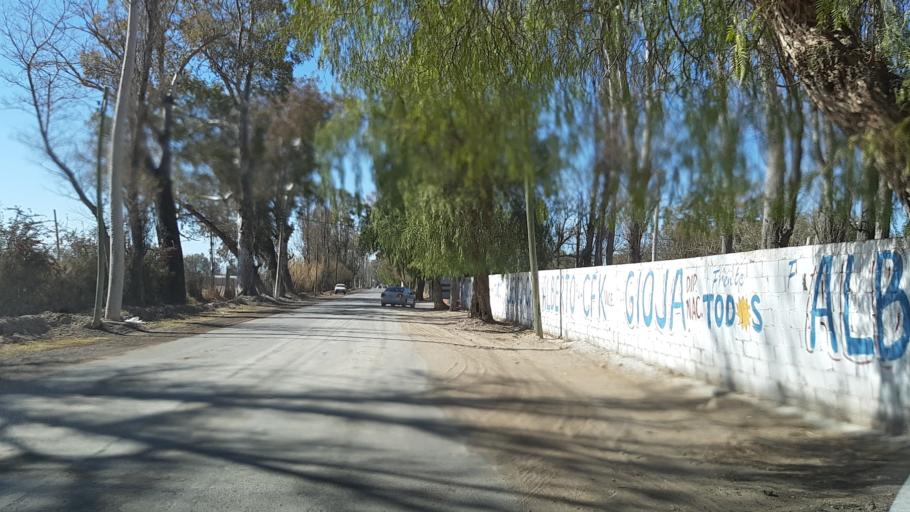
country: AR
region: San Juan
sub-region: Departamento de Zonda
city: Zonda
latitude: -31.4696
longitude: -68.7482
